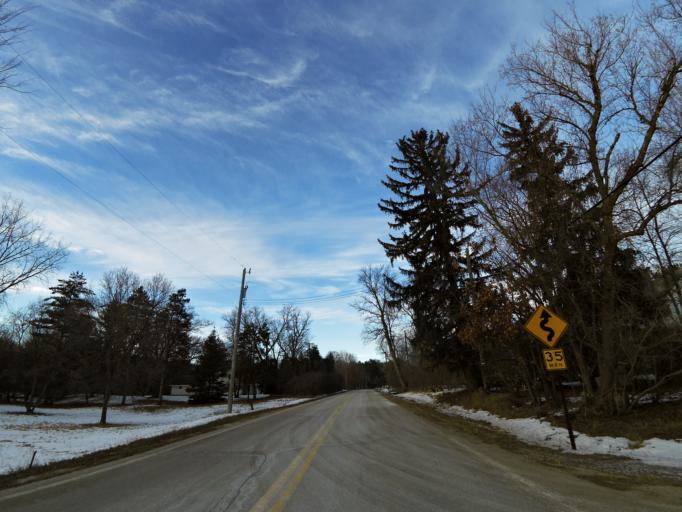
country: US
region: Minnesota
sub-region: Washington County
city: Afton
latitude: 44.9259
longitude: -92.8020
